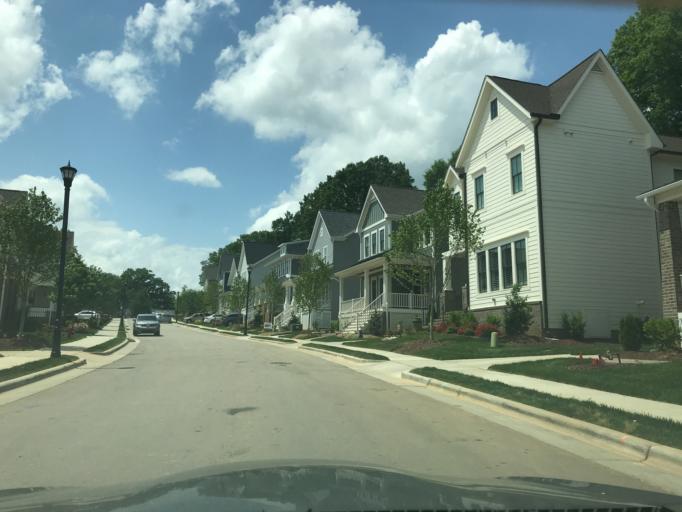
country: US
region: North Carolina
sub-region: Wake County
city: Raleigh
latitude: 35.7922
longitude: -78.6272
